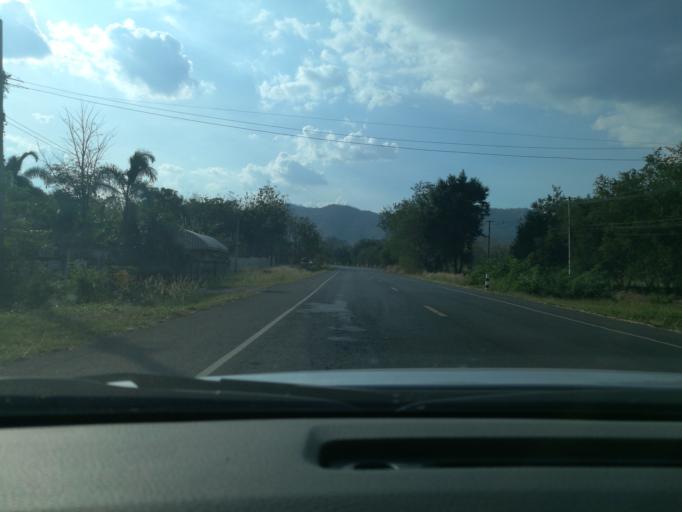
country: TH
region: Phetchabun
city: Phetchabun
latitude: 16.5485
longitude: 101.1281
